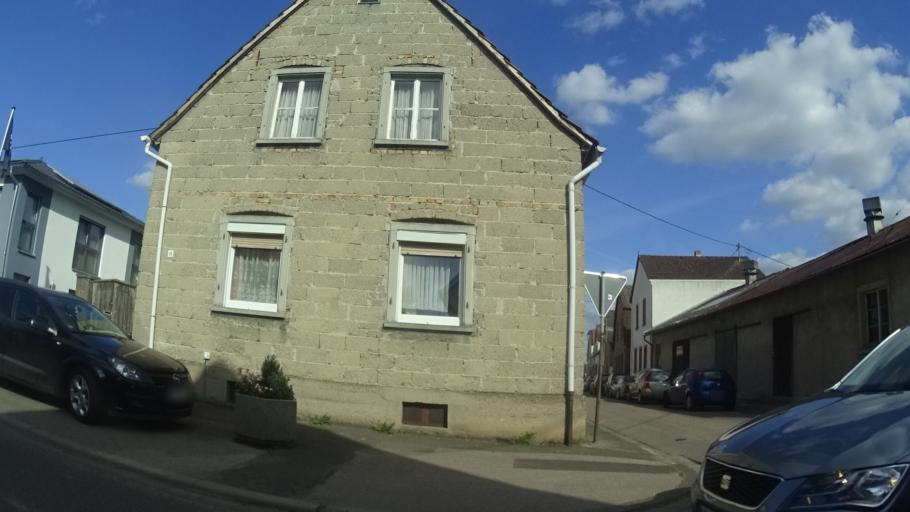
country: DE
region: Rheinland-Pfalz
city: Alsheim
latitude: 49.7688
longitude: 8.3417
